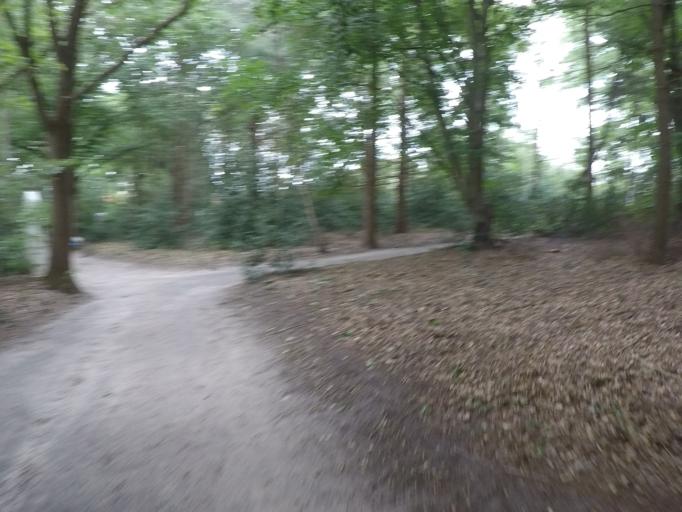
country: BE
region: Flanders
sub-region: Provincie Antwerpen
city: Grobbendonk
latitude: 51.1994
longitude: 4.7060
